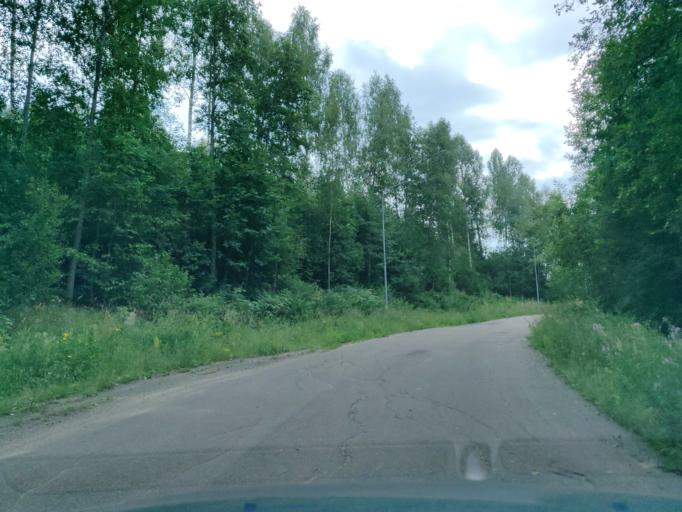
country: SE
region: Vaermland
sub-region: Munkfors Kommun
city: Munkfors
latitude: 59.8509
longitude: 13.5607
